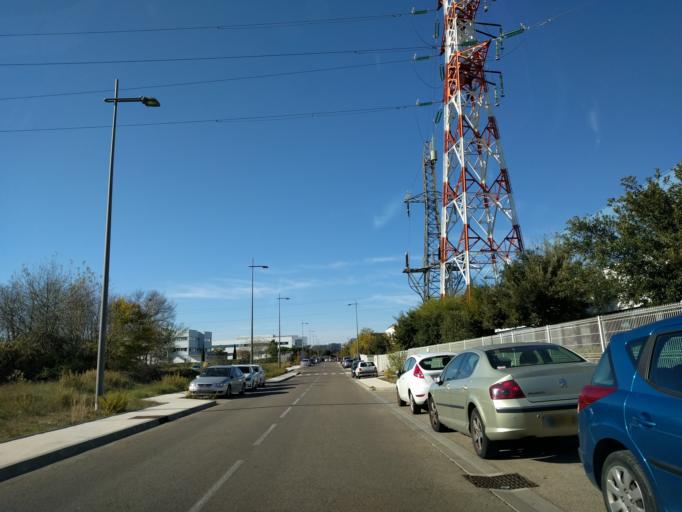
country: FR
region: Languedoc-Roussillon
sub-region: Departement de l'Herault
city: Castelnau-le-Lez
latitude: 43.6178
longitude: 3.9183
